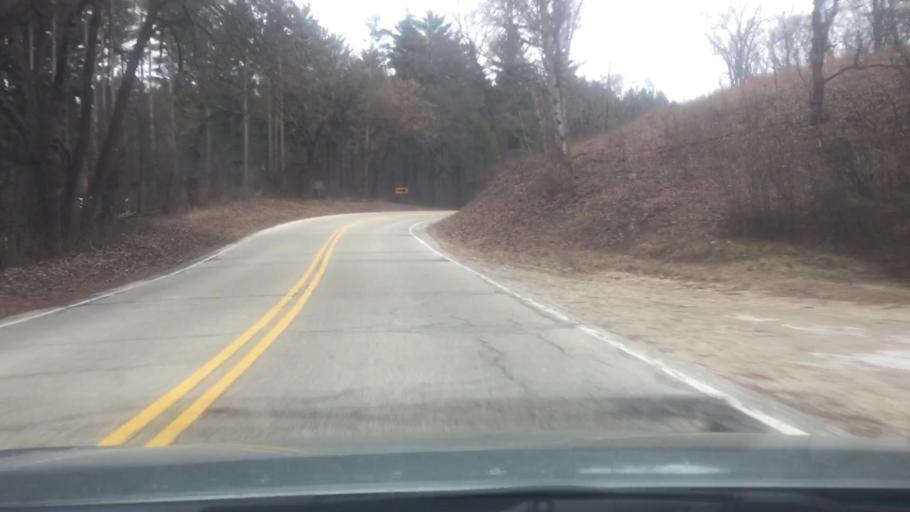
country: US
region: Wisconsin
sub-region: Waukesha County
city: North Prairie
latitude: 42.9418
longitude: -88.4585
